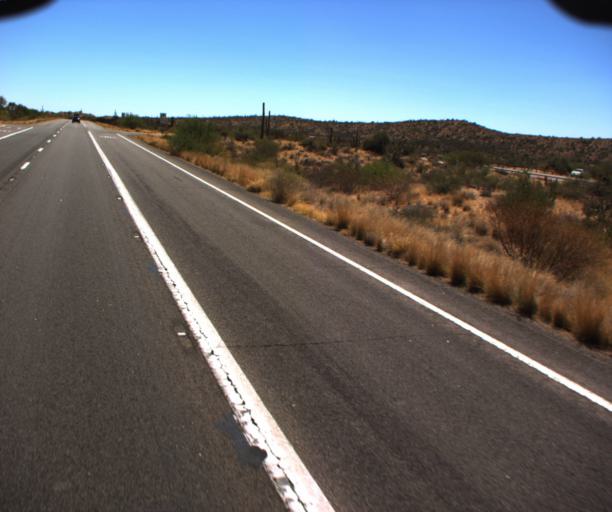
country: US
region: Arizona
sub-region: Maricopa County
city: Rio Verde
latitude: 33.6793
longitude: -111.5026
